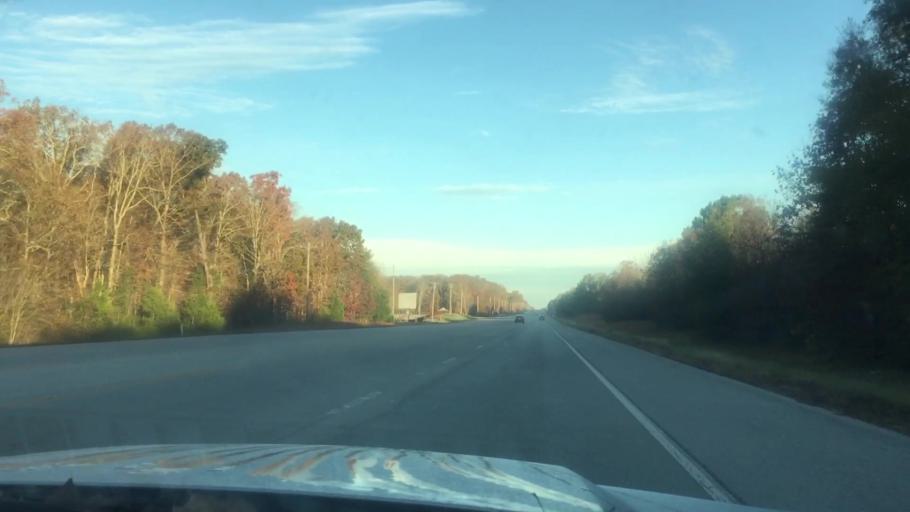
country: US
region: Tennessee
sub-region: Franklin County
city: Estill Springs
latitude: 35.3099
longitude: -86.1626
